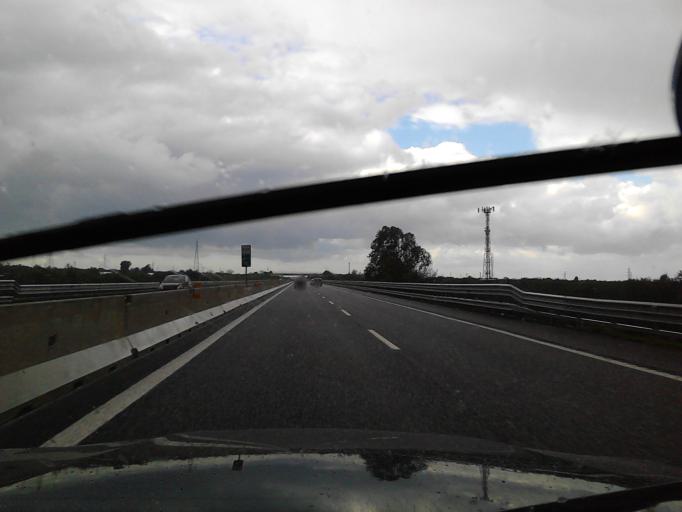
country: IT
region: Apulia
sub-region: Provincia di Bari
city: Molfetta
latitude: 41.1629
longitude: 16.6257
